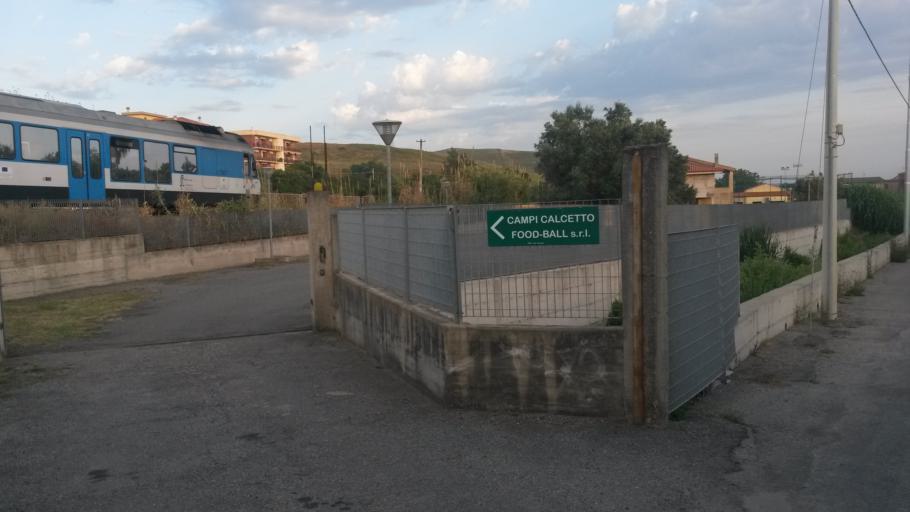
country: IT
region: Calabria
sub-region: Provincia di Catanzaro
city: Catanzaro
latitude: 38.8852
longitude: 16.6023
